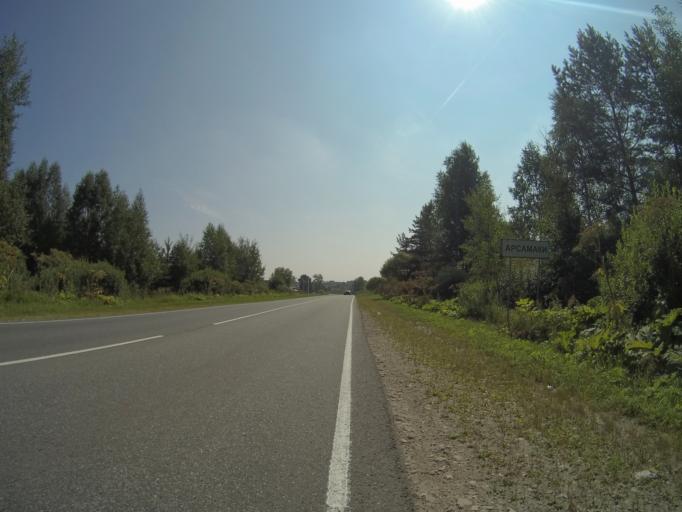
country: RU
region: Vladimir
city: Anopino
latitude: 55.7438
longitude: 40.6922
